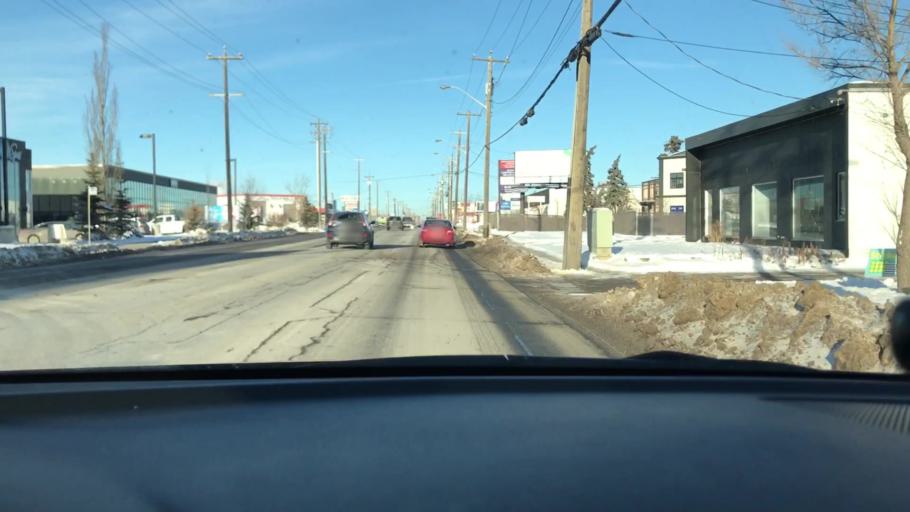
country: CA
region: Alberta
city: Edmonton
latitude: 53.4917
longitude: -113.4861
